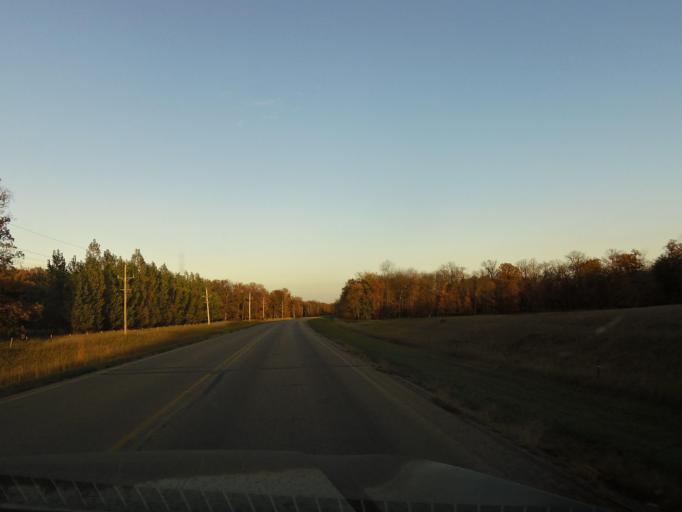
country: CA
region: Manitoba
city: Altona
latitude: 48.9637
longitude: -97.4287
